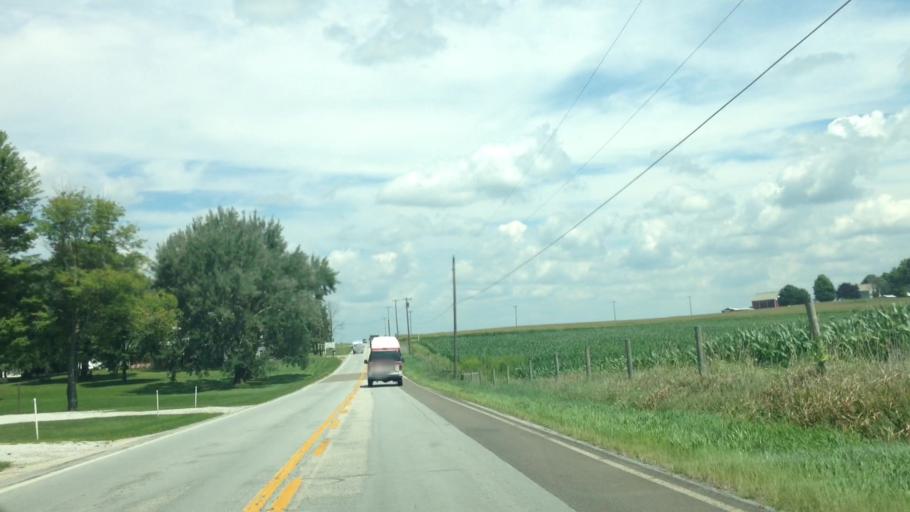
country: US
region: Ohio
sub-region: Wayne County
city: Orrville
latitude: 40.9066
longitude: -81.7998
